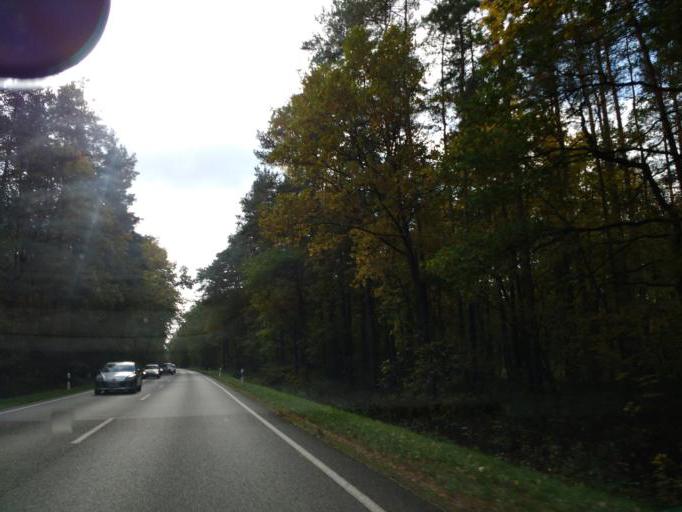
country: DE
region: Brandenburg
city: Petershagen
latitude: 52.5101
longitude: 13.8017
